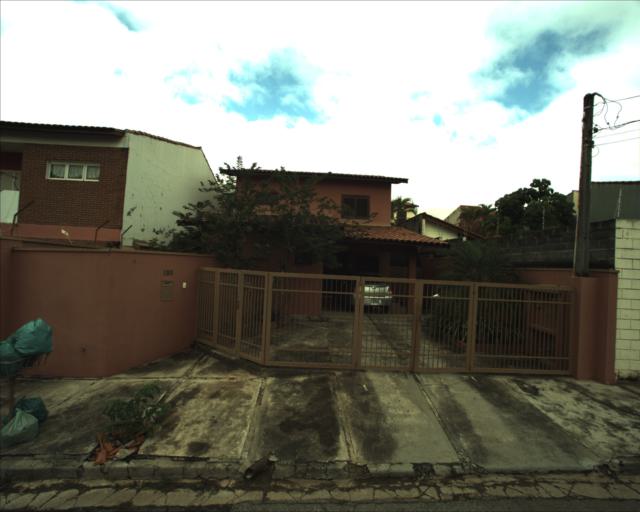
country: BR
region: Sao Paulo
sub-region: Sorocaba
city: Sorocaba
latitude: -23.5282
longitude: -47.4635
